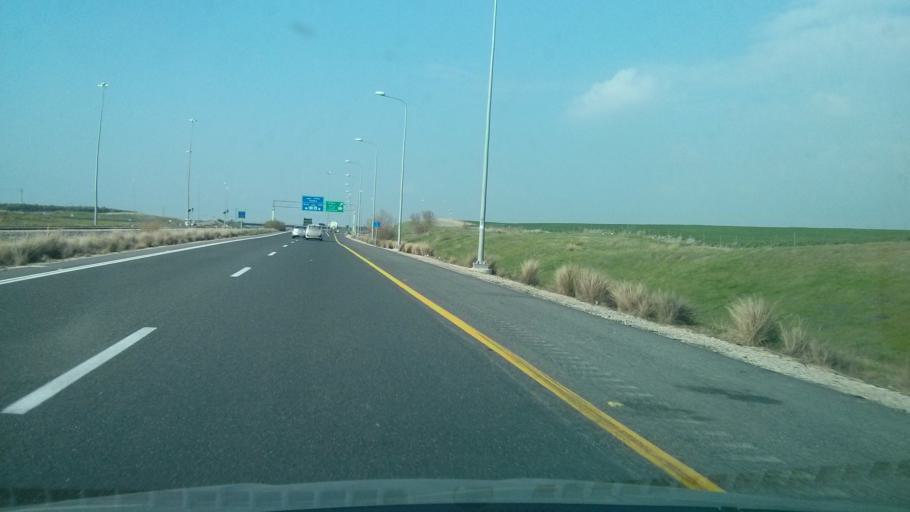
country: IL
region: Central District
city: Gedera
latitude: 31.7853
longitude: 34.8331
